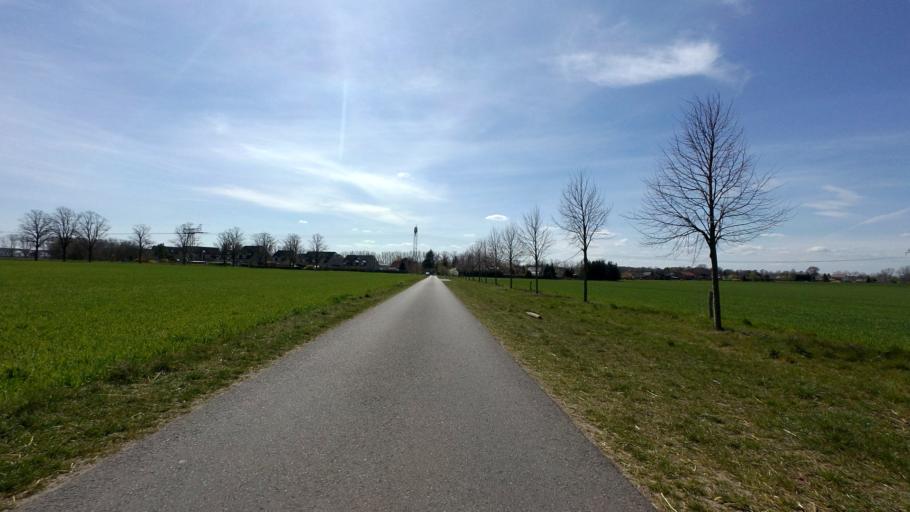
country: DE
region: Brandenburg
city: Schonefeld
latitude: 52.3460
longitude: 13.5206
